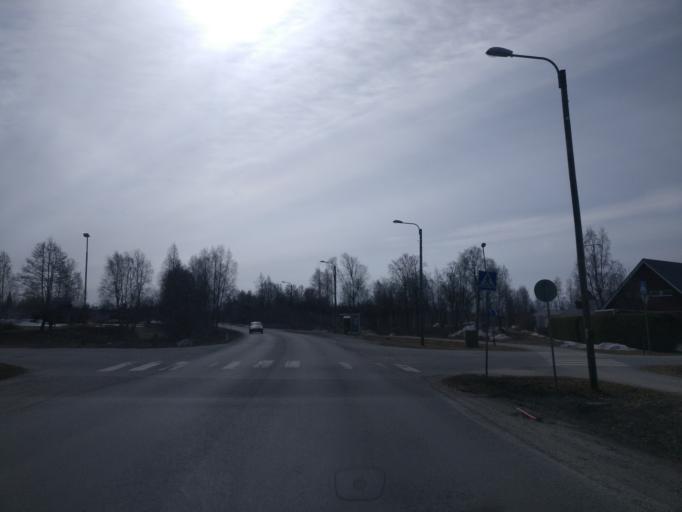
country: FI
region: Lapland
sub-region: Kemi-Tornio
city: Kemi
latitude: 65.7553
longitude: 24.5498
